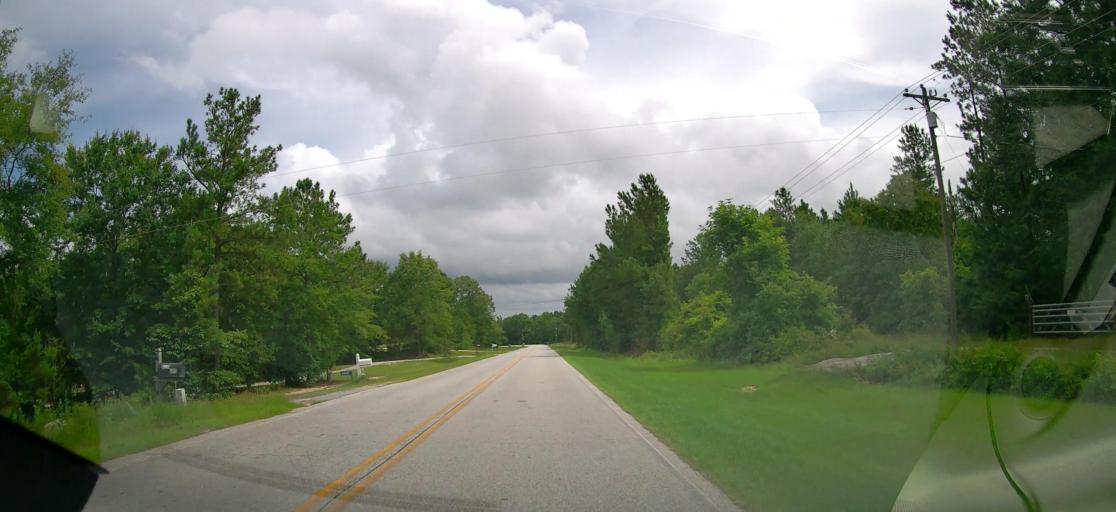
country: US
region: Georgia
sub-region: Peach County
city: Byron
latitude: 32.7089
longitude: -83.7807
